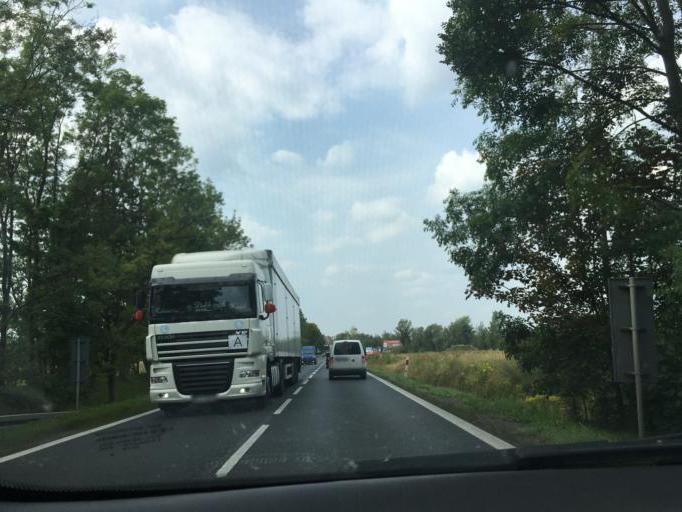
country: PL
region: Silesian Voivodeship
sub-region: Powiat bierunsko-ledzinski
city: Bierun
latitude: 50.0839
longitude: 19.1244
